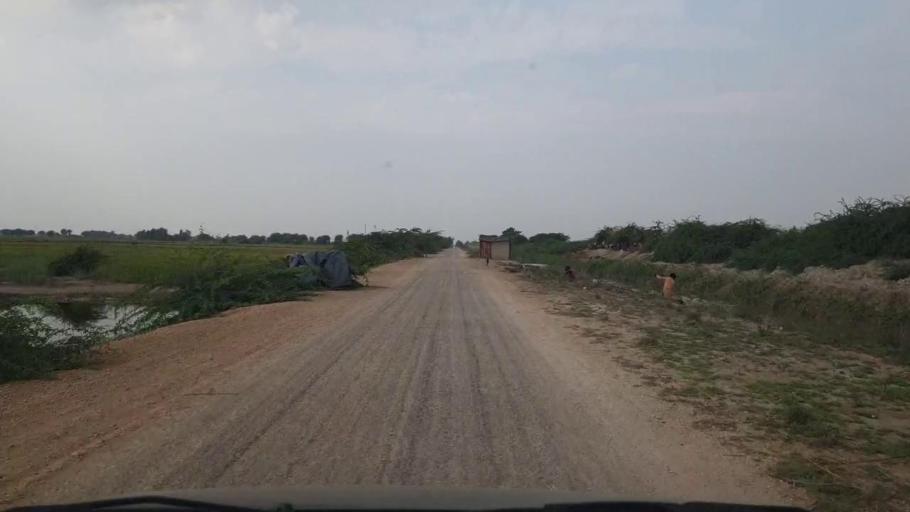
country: PK
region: Sindh
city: Kario
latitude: 24.6025
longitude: 68.6008
